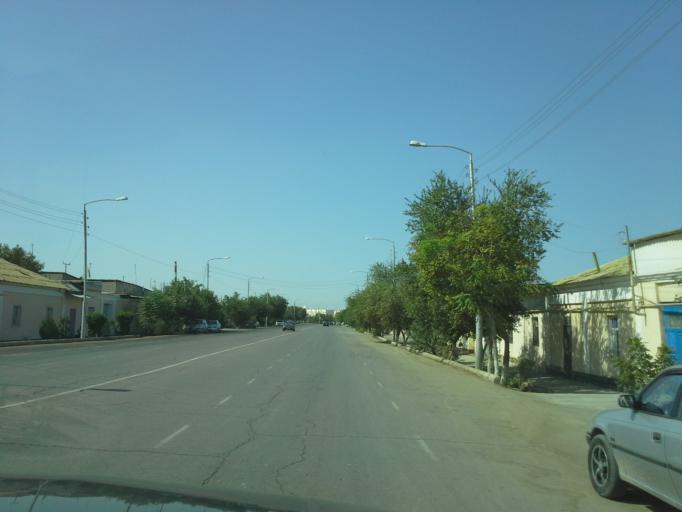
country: TM
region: Dasoguz
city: Dasoguz
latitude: 41.8212
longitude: 59.9799
